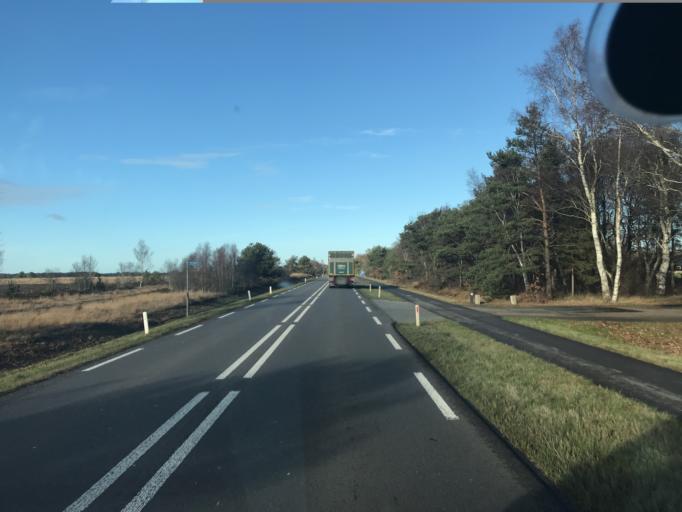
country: NL
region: Gelderland
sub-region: Gemeente Apeldoorn
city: Uddel
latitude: 52.2613
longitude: 5.7418
